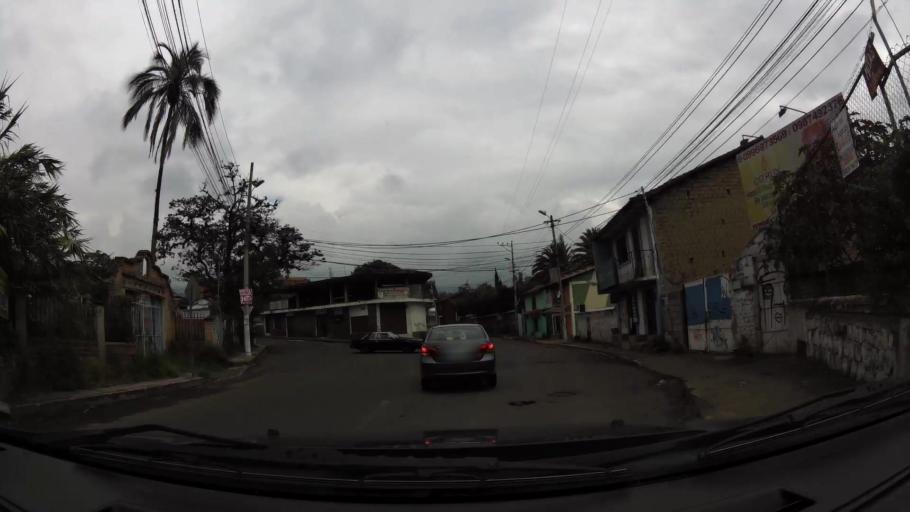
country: EC
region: Pichincha
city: Sangolqui
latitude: -0.3001
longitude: -78.4648
